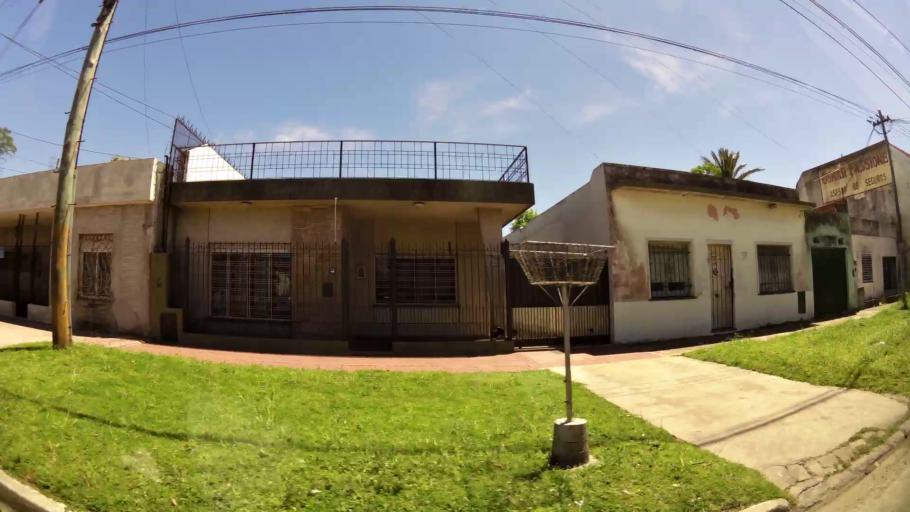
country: AR
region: Buenos Aires
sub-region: Partido de Quilmes
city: Quilmes
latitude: -34.7380
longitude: -58.2902
